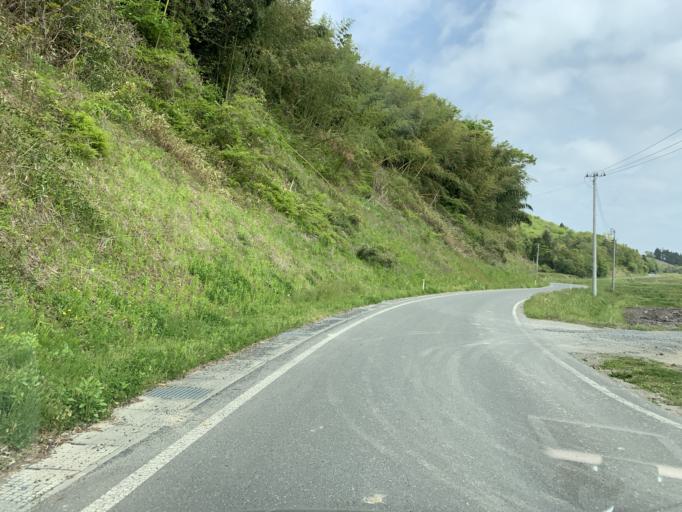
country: JP
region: Iwate
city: Ichinoseki
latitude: 38.8548
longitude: 141.1965
